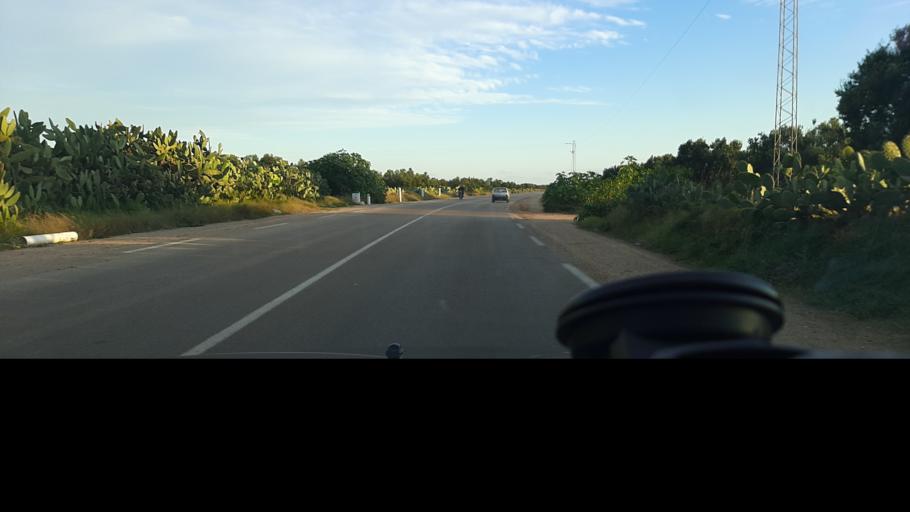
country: TN
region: Safaqis
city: Sfax
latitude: 34.9295
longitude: 10.6224
